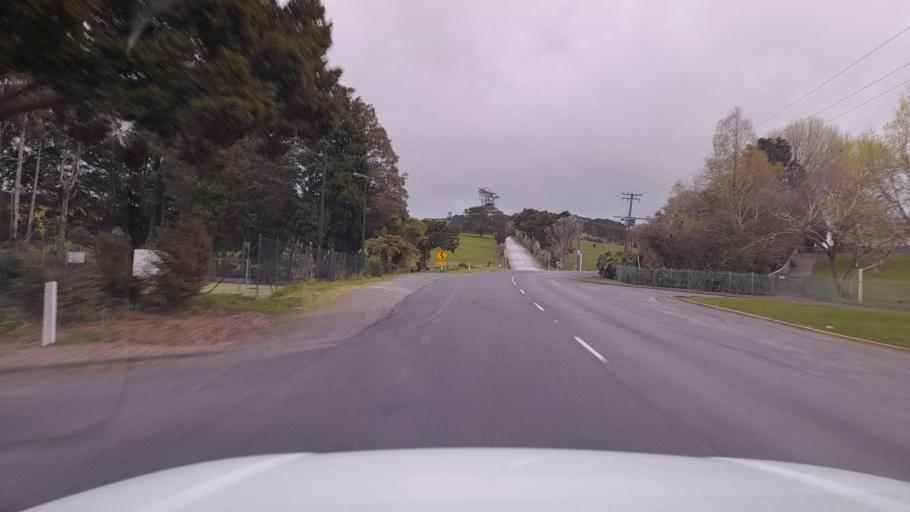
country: NZ
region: Northland
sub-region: Whangarei
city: Maungatapere
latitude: -35.6587
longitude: 174.2224
